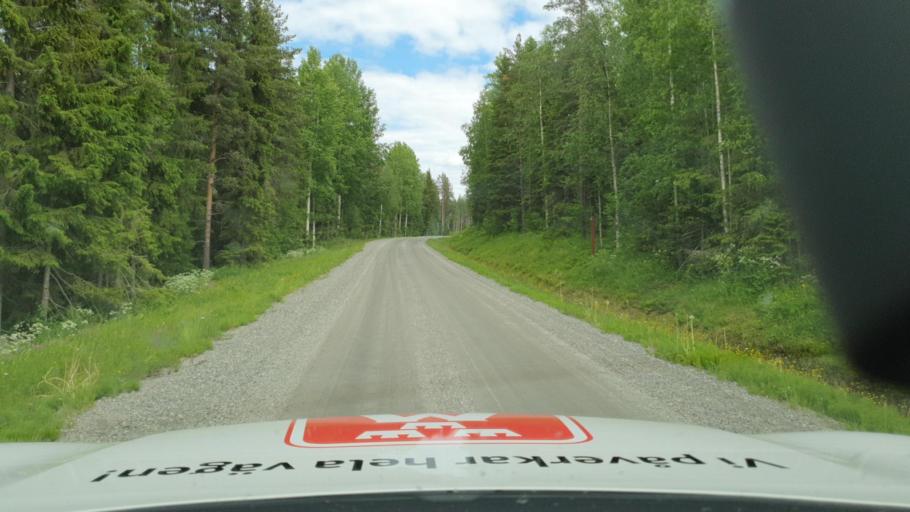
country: SE
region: Vaesterbotten
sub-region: Norsjo Kommun
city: Norsjoe
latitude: 64.8074
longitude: 19.6053
